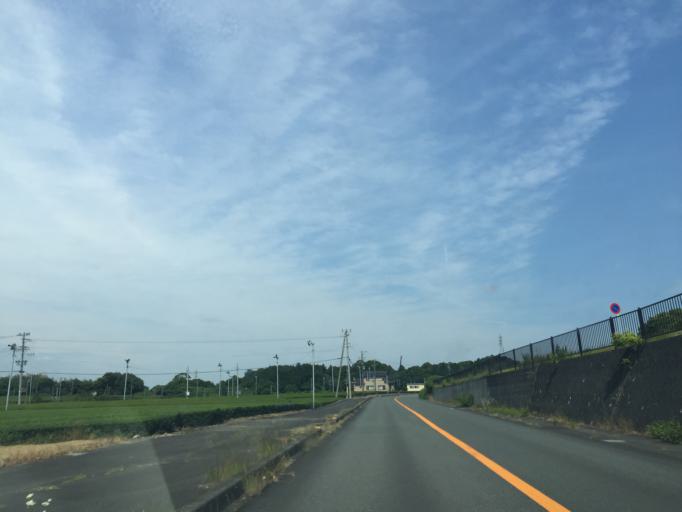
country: JP
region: Shizuoka
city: Kakegawa
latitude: 34.7543
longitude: 137.9821
